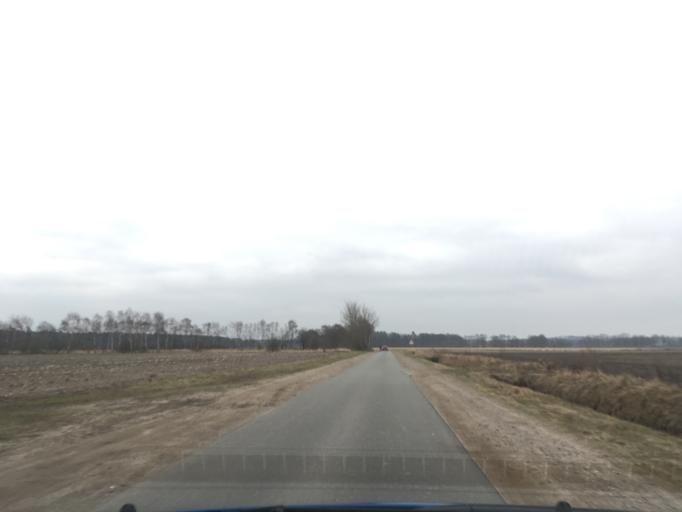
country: DE
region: Lower Saxony
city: Mechtersen
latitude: 53.2998
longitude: 10.3296
